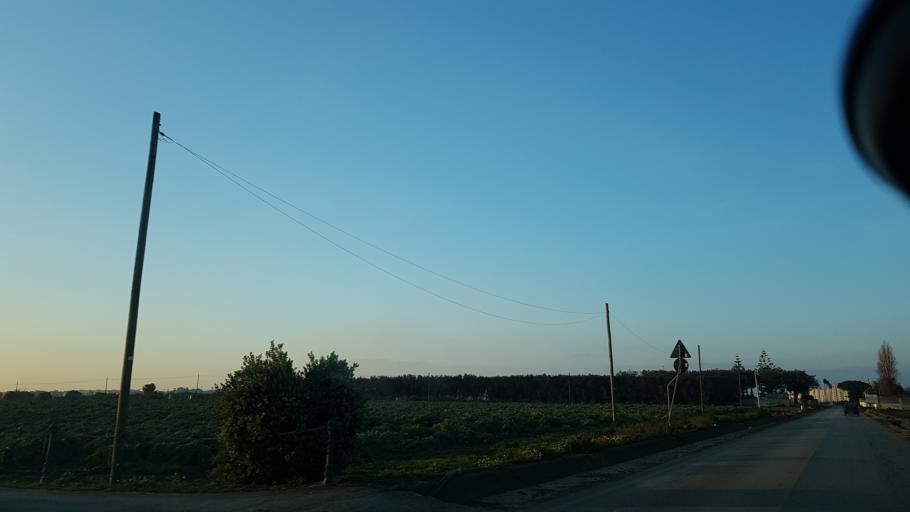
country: IT
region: Apulia
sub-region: Provincia di Brindisi
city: La Rosa
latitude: 40.6077
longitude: 17.9448
